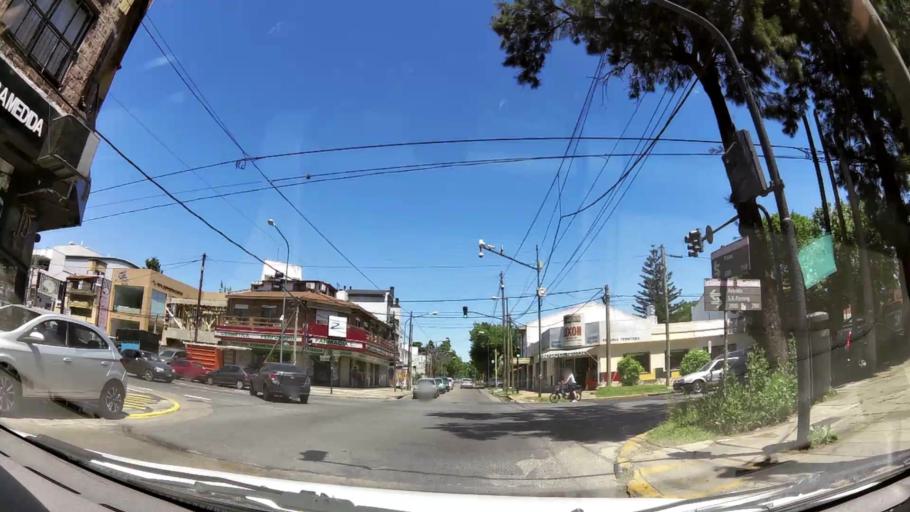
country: AR
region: Buenos Aires
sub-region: Partido de Vicente Lopez
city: Olivos
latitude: -34.5060
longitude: -58.5157
